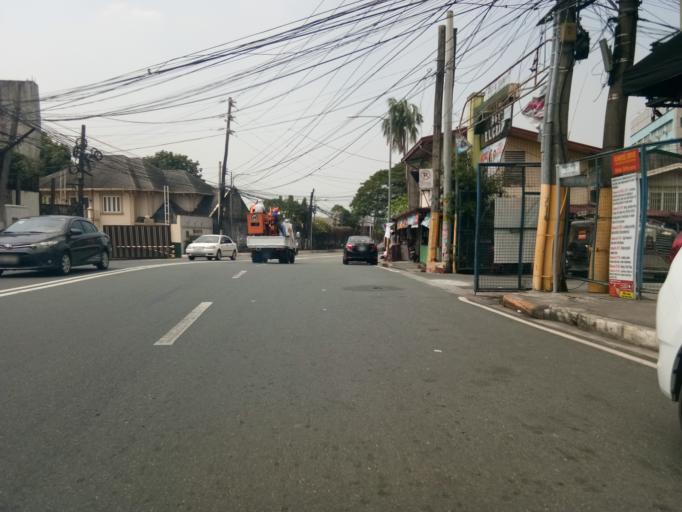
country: PH
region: Metro Manila
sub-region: San Juan
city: San Juan
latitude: 14.6088
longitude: 121.0461
